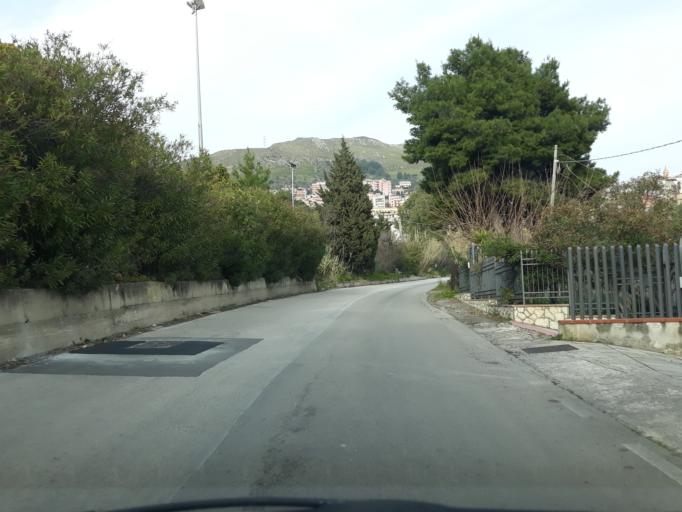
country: IT
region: Sicily
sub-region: Palermo
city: Giardinello
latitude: 38.0865
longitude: 13.1647
